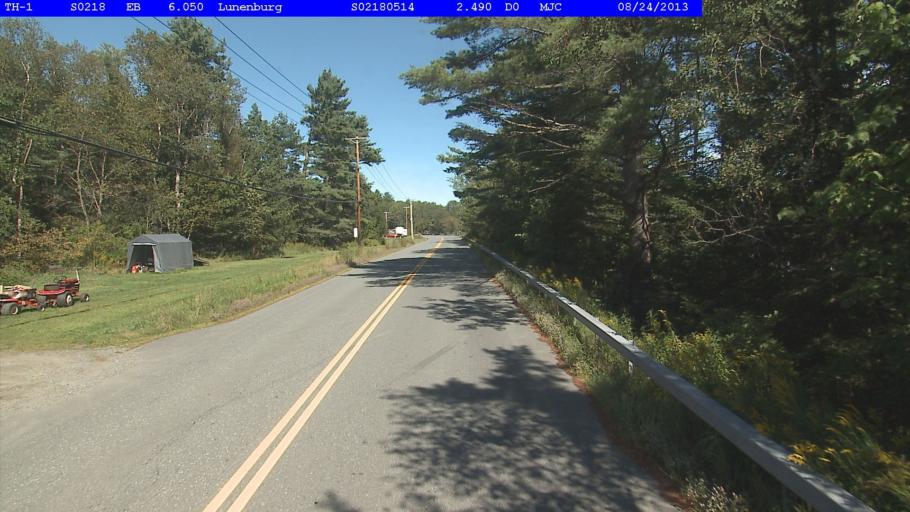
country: US
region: New Hampshire
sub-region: Coos County
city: Whitefield
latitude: 44.4153
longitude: -71.7048
